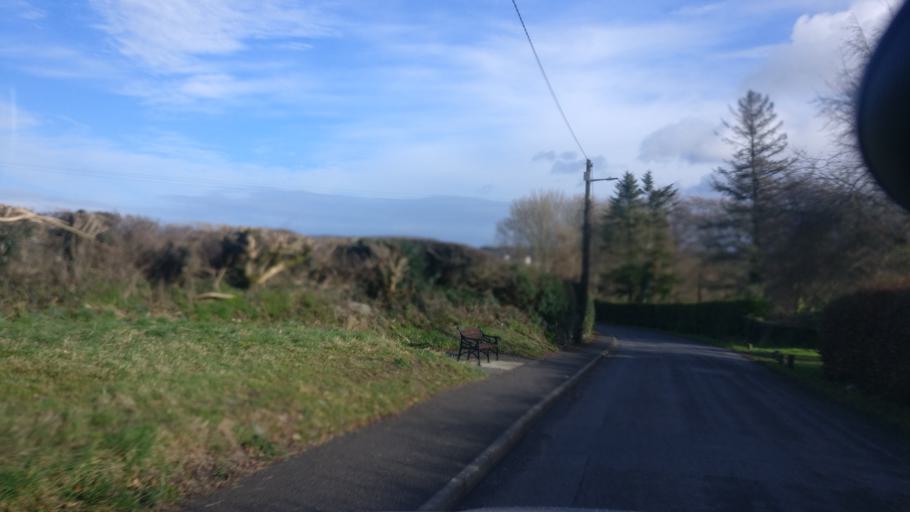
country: IE
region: Leinster
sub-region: Kilkenny
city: Thomastown
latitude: 52.5226
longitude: -7.1454
